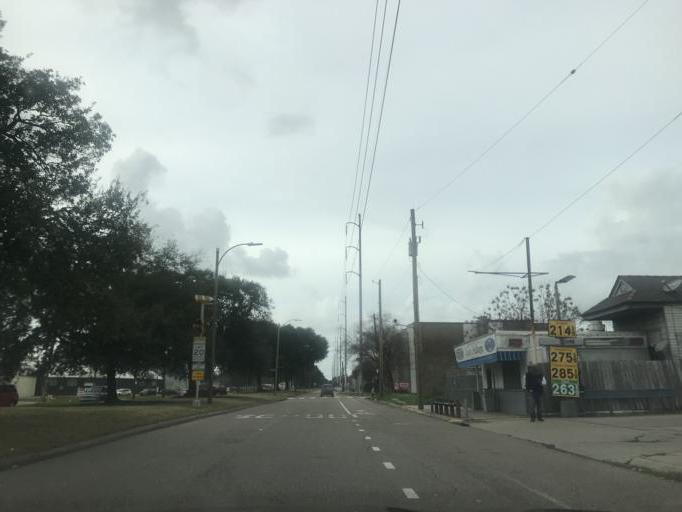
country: US
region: Louisiana
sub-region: Orleans Parish
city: New Orleans
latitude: 29.9466
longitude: -90.0887
